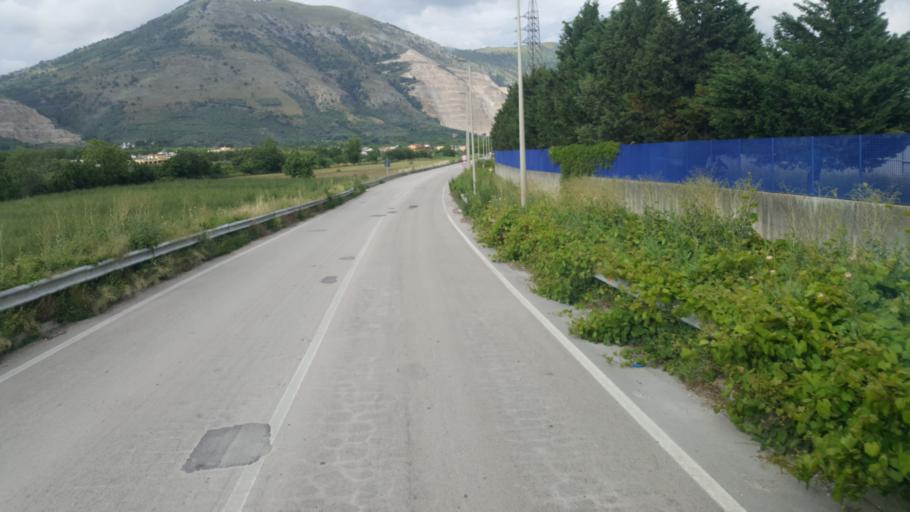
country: IT
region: Campania
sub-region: Provincia di Caserta
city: San Felice A Cancello
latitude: 40.9759
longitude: 14.4590
